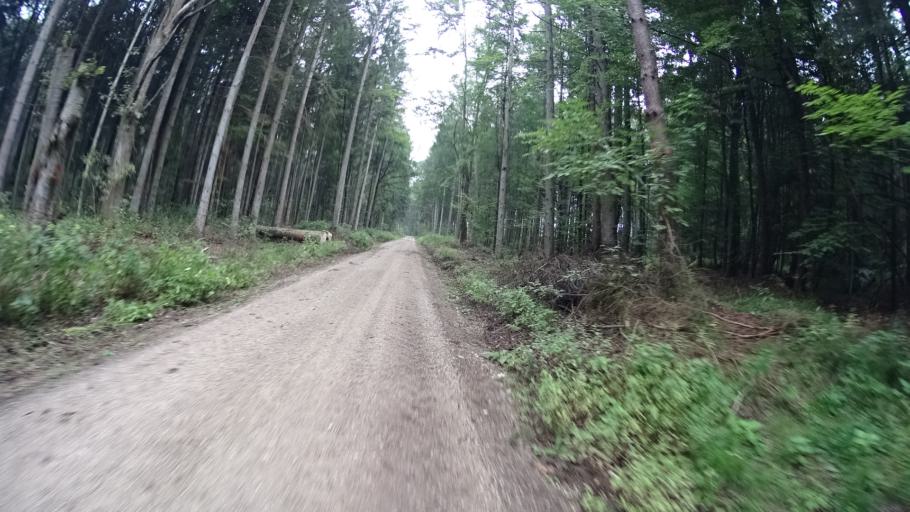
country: DE
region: Bavaria
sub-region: Upper Bavaria
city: Stammham
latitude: 48.8554
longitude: 11.4943
